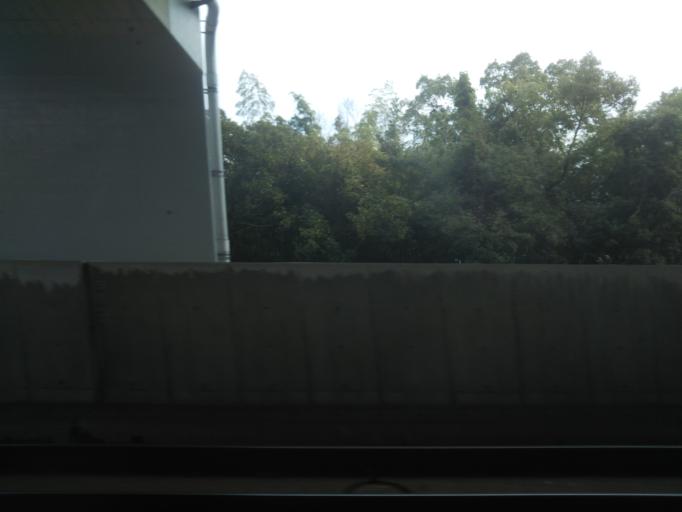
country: JP
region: Kagawa
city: Sakaidecho
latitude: 34.4231
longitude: 133.8040
